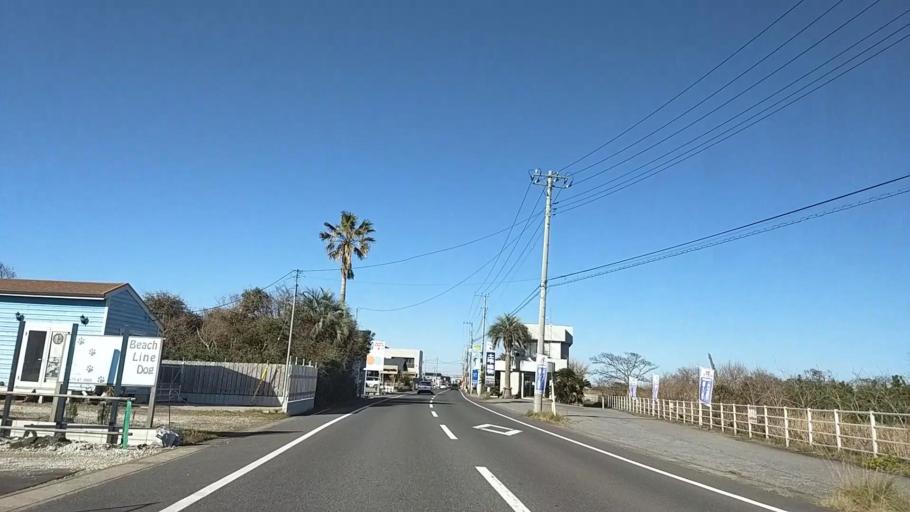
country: JP
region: Chiba
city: Ohara
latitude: 35.3520
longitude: 140.3895
